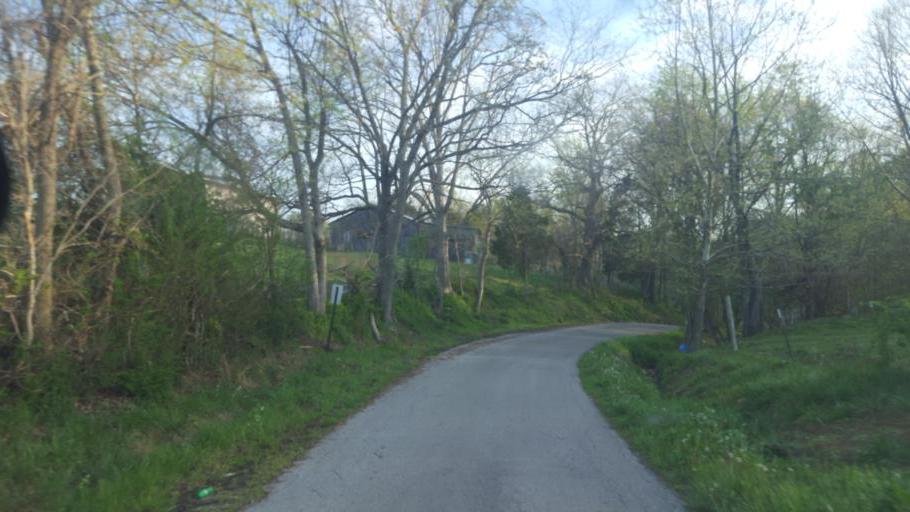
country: US
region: Kentucky
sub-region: Barren County
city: Cave City
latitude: 37.2160
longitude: -86.0002
